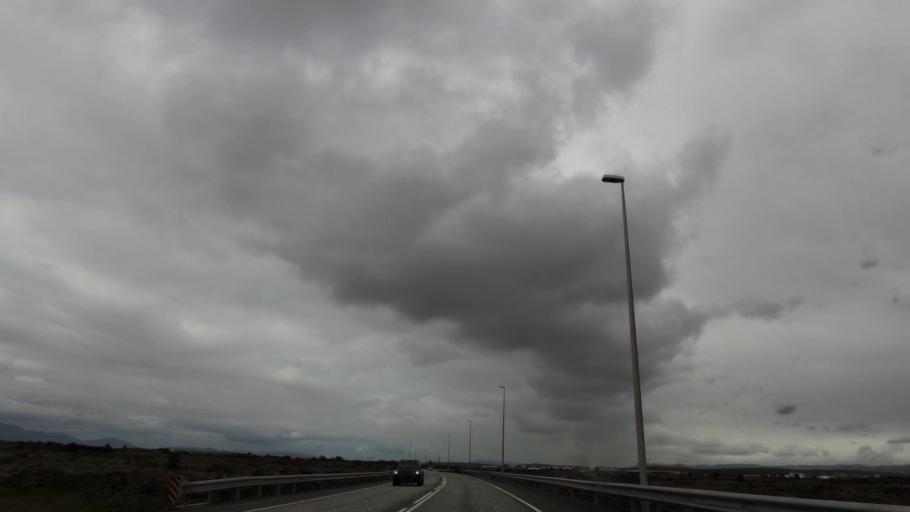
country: IS
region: Capital Region
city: Alftanes
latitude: 64.0907
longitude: -21.9783
